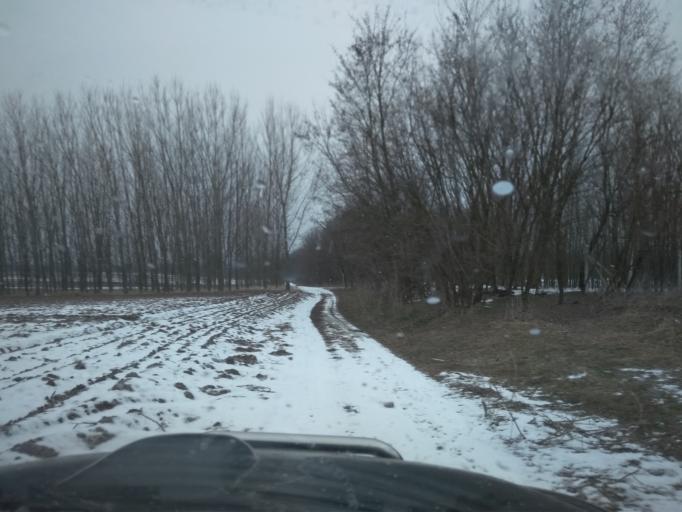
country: HU
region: Szabolcs-Szatmar-Bereg
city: Apagy
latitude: 47.9789
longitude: 21.9133
